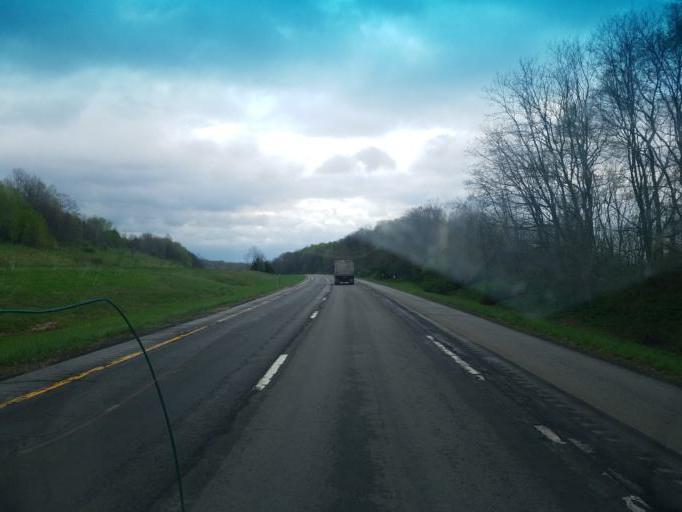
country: US
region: New York
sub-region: Chautauqua County
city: Lakewood
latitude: 42.1298
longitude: -79.3241
